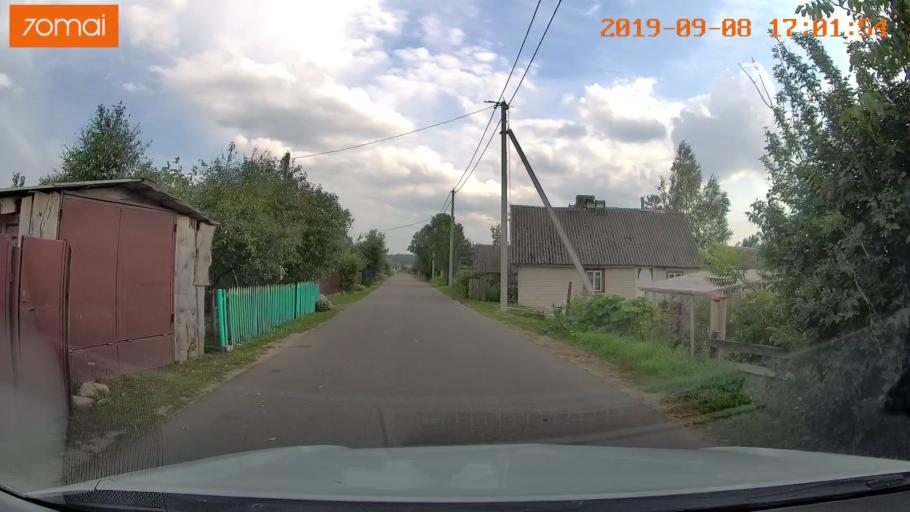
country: BY
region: Grodnenskaya
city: Hrodna
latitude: 53.7068
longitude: 23.9365
